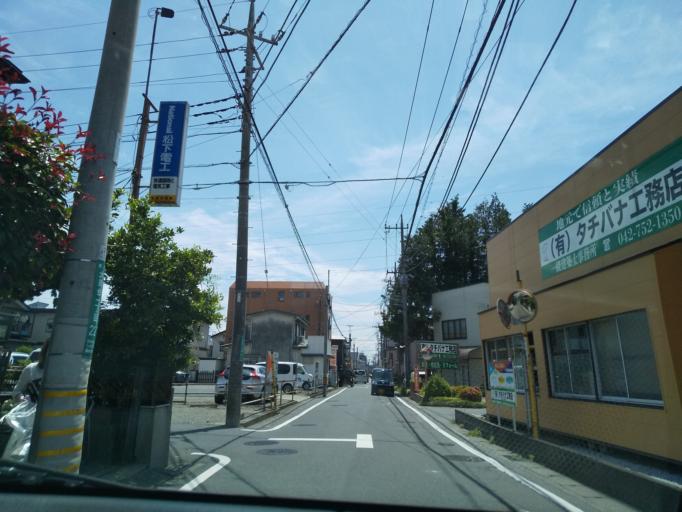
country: JP
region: Tokyo
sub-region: Machida-shi
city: Machida
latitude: 35.5556
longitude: 139.3998
